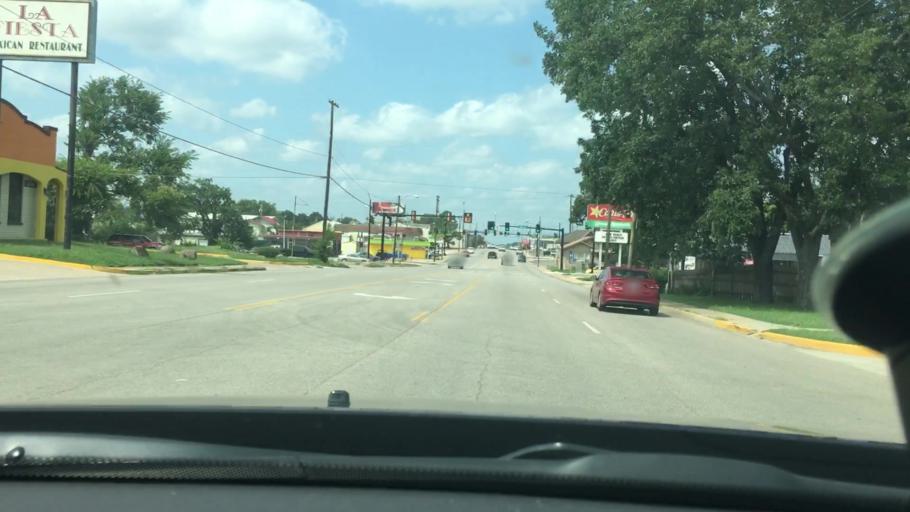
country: US
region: Oklahoma
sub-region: Pontotoc County
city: Ada
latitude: 34.7722
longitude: -96.6699
